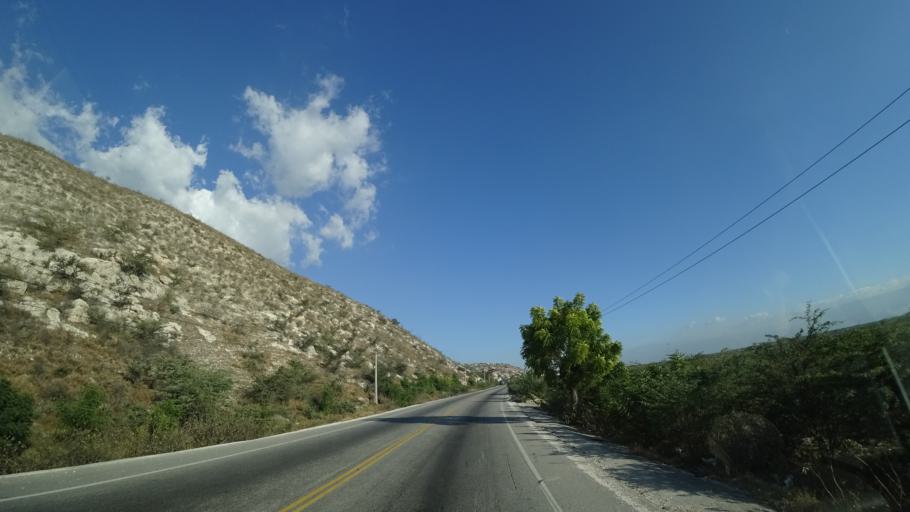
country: HT
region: Ouest
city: Delmas 73
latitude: 18.6704
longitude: -72.3051
